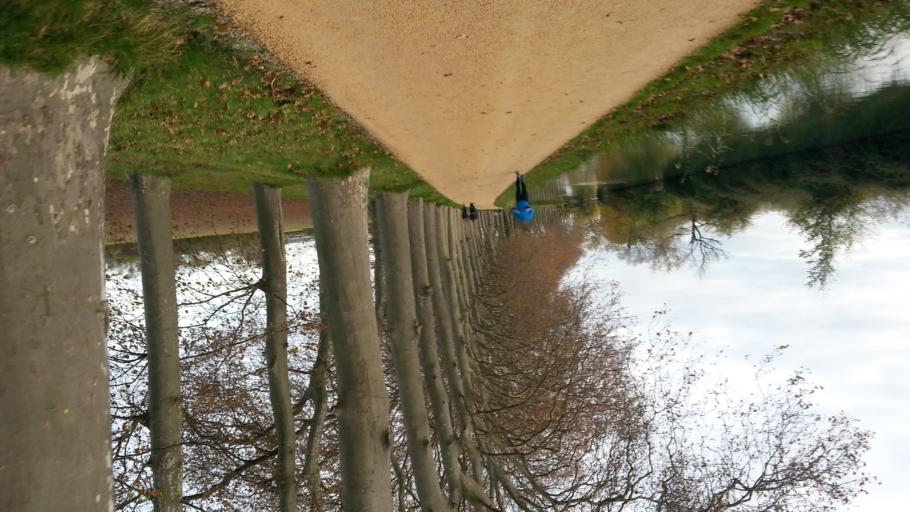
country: FR
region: Midi-Pyrenees
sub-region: Departement de la Haute-Garonne
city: Castanet-Tolosan
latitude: 43.5348
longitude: 1.5049
